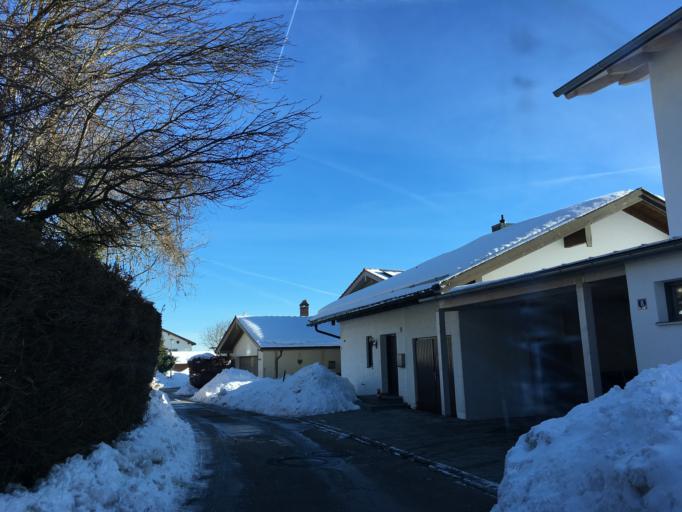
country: DE
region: Bavaria
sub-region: Upper Bavaria
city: Aschau im Chiemgau
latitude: 47.8066
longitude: 12.3201
